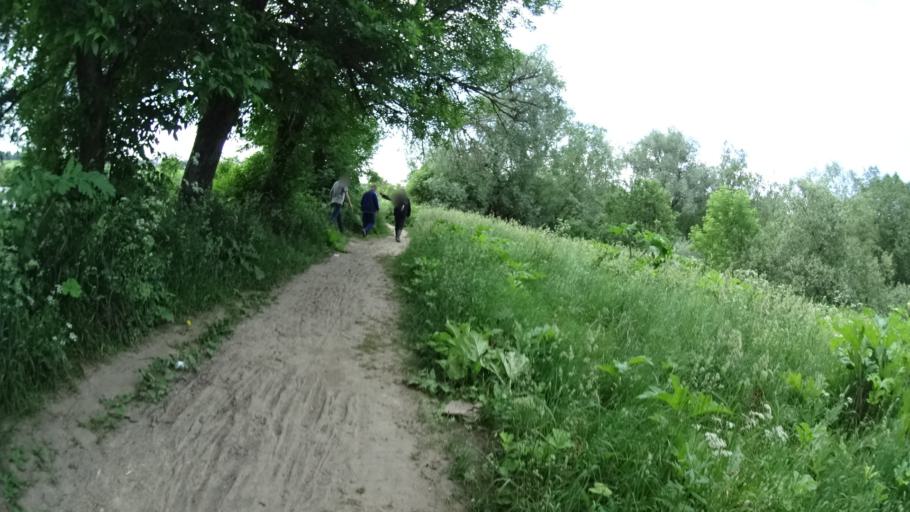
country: RU
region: Moskovskaya
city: Zelenogradskiy
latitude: 56.0847
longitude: 37.9087
